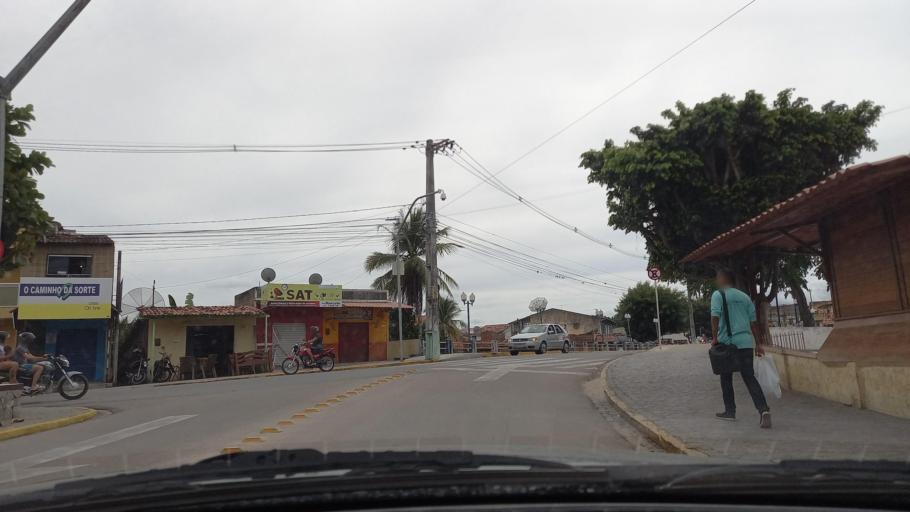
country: BR
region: Pernambuco
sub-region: Gravata
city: Gravata
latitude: -8.2013
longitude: -35.5709
